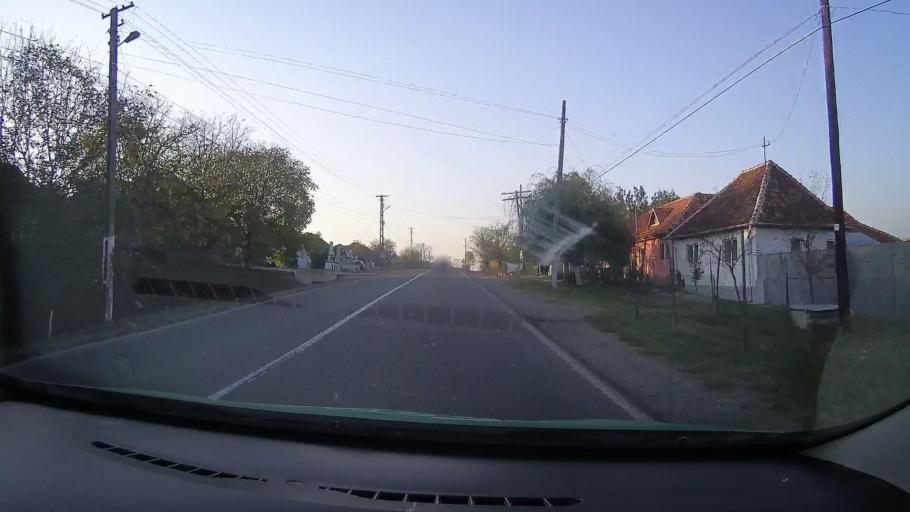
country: RO
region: Arad
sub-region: Comuna Barsa
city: Barsa
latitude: 46.3971
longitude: 22.0343
